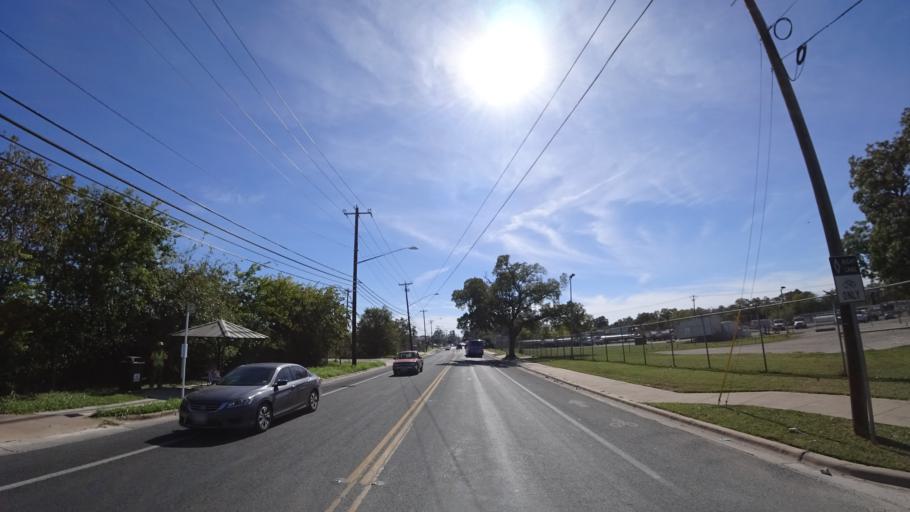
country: US
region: Texas
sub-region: Travis County
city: Austin
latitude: 30.2674
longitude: -97.6944
